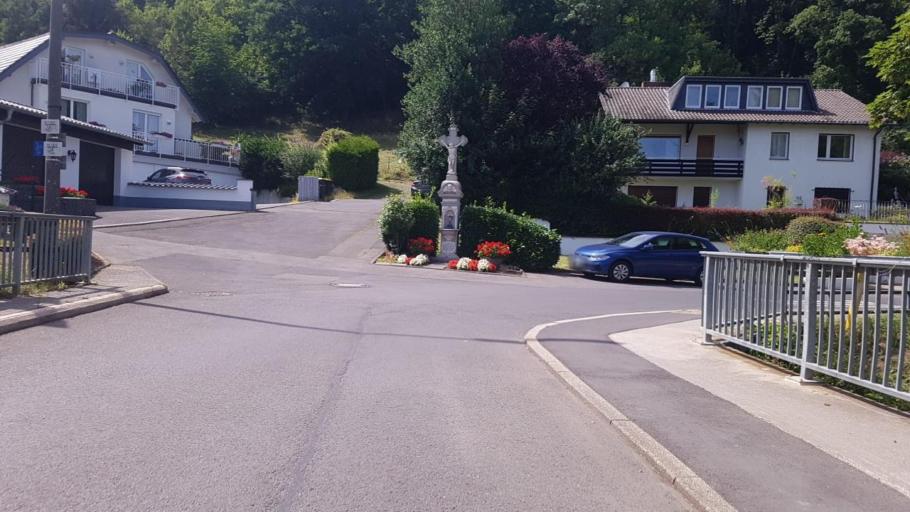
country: DE
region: North Rhine-Westphalia
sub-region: Regierungsbezirk Koln
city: Konigswinter
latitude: 50.6393
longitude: 7.1713
